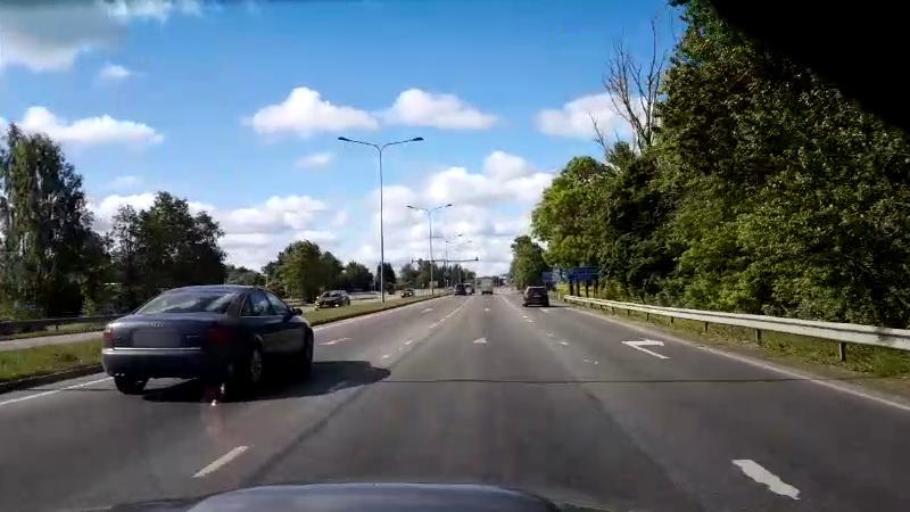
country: EE
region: Harju
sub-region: Saue vald
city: Laagri
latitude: 59.3501
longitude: 24.6271
